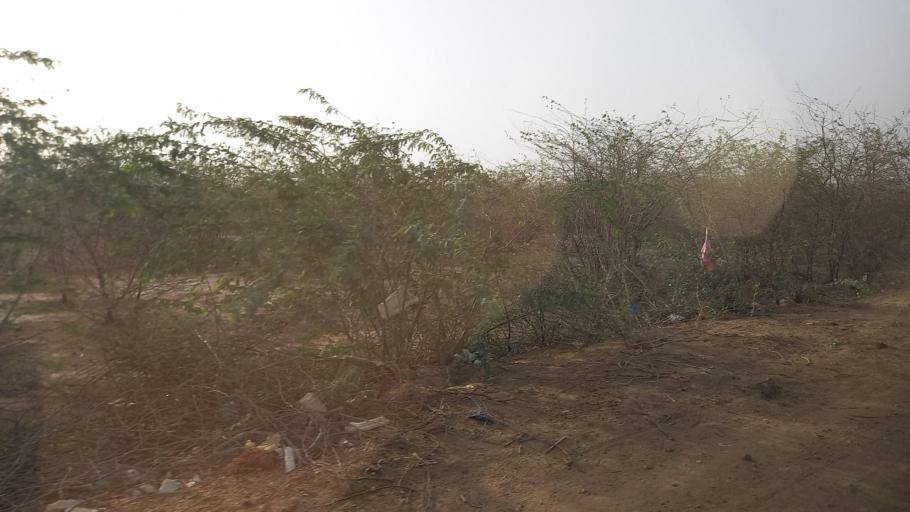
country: PK
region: Sindh
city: Malir Cantonment
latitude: 25.1152
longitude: 67.1915
